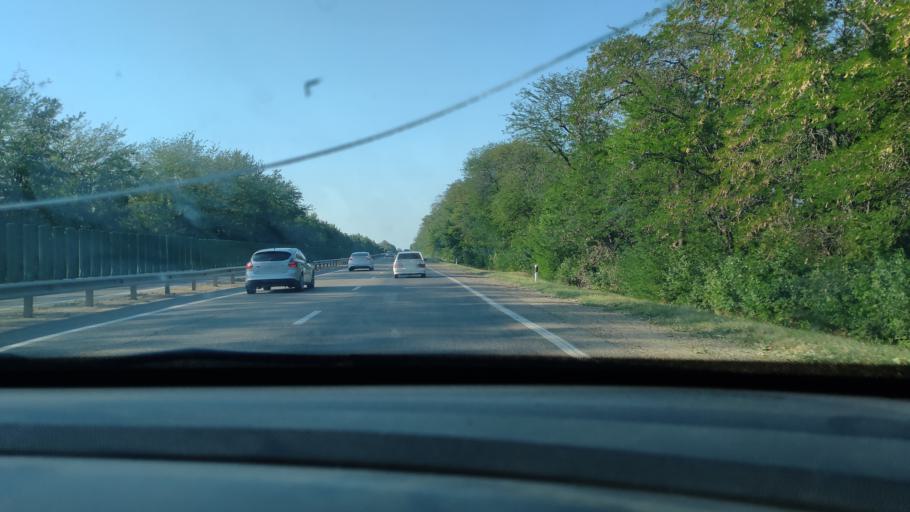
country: RU
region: Krasnodarskiy
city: Timashevsk
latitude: 45.5280
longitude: 38.9414
